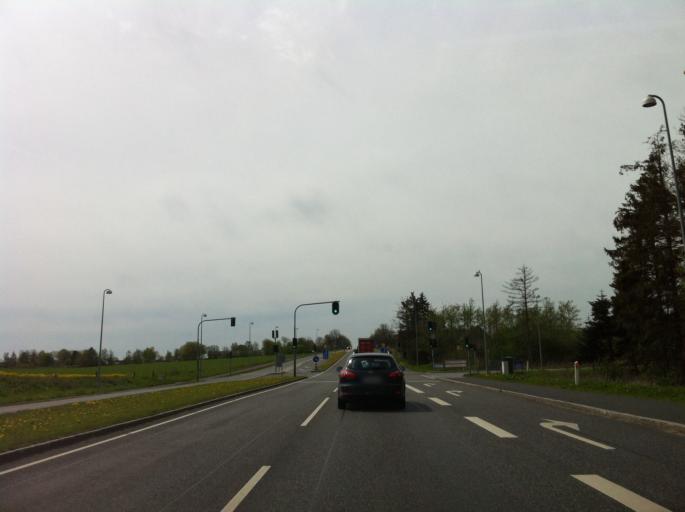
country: DK
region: Zealand
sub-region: Lejre Kommune
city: Osted
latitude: 55.5703
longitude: 11.9772
